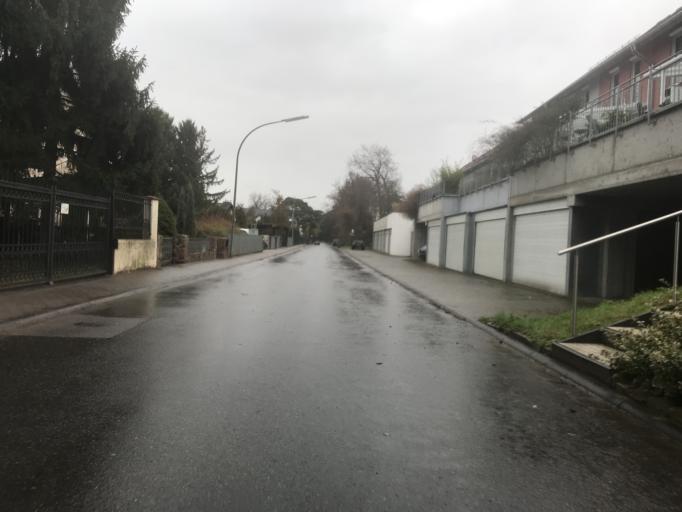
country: DE
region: Hesse
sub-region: Regierungsbezirk Darmstadt
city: Eltville
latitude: 50.0063
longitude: 8.1376
